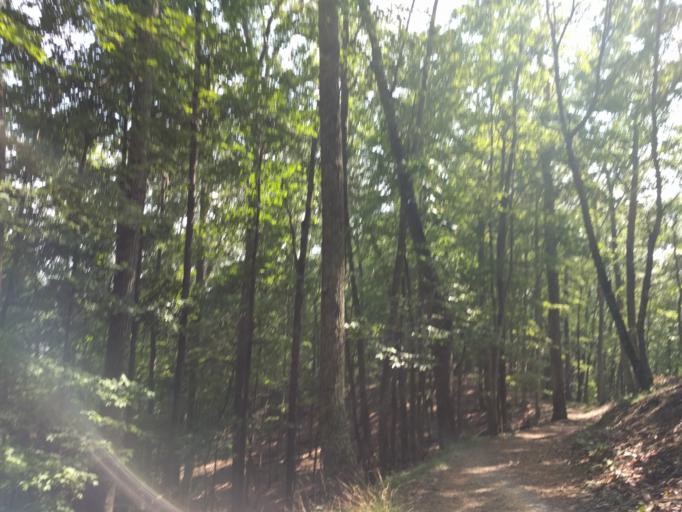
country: US
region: Virginia
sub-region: Smyth County
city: Marion
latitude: 36.8844
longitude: -81.5200
